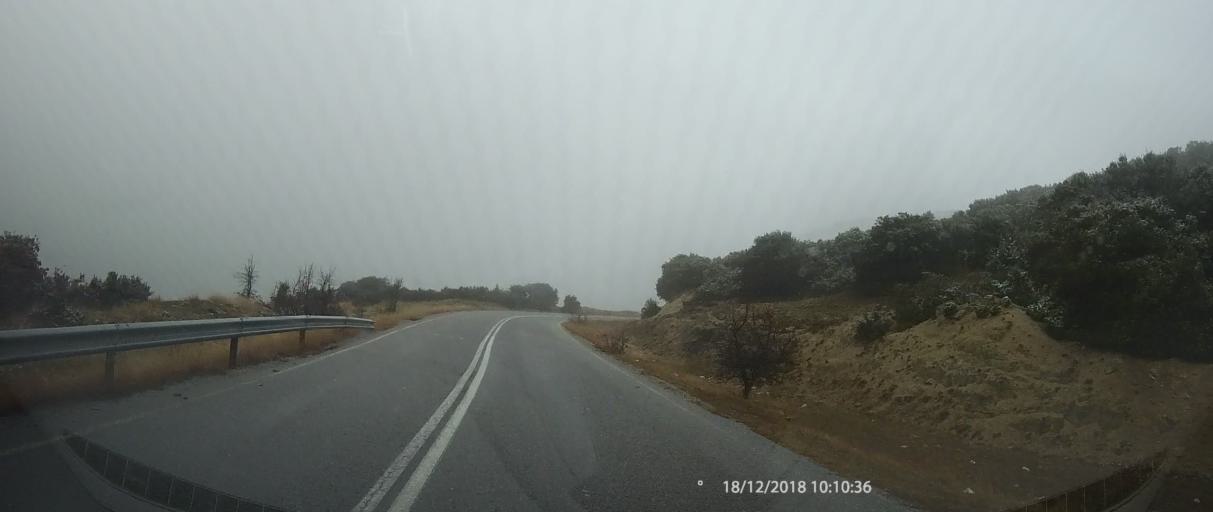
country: GR
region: Thessaly
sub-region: Nomos Larisis
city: Livadi
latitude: 40.0902
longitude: 22.2111
